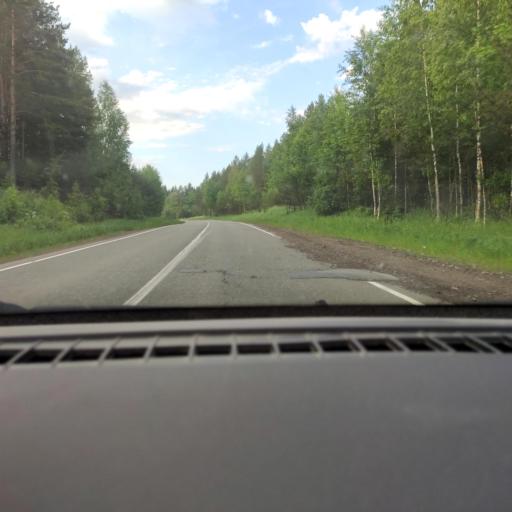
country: RU
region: Udmurtiya
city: Votkinsk
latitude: 57.1633
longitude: 54.1225
